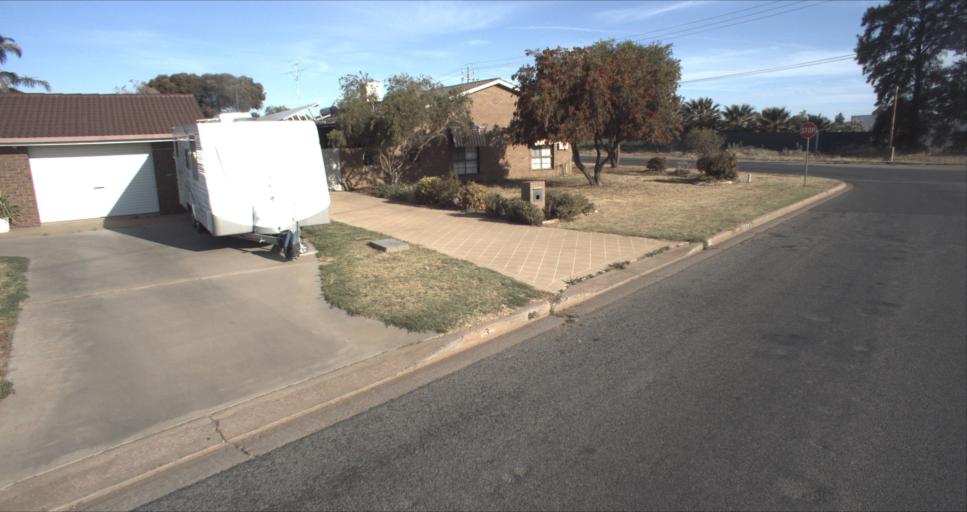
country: AU
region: New South Wales
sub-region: Leeton
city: Leeton
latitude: -34.5460
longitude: 146.3988
